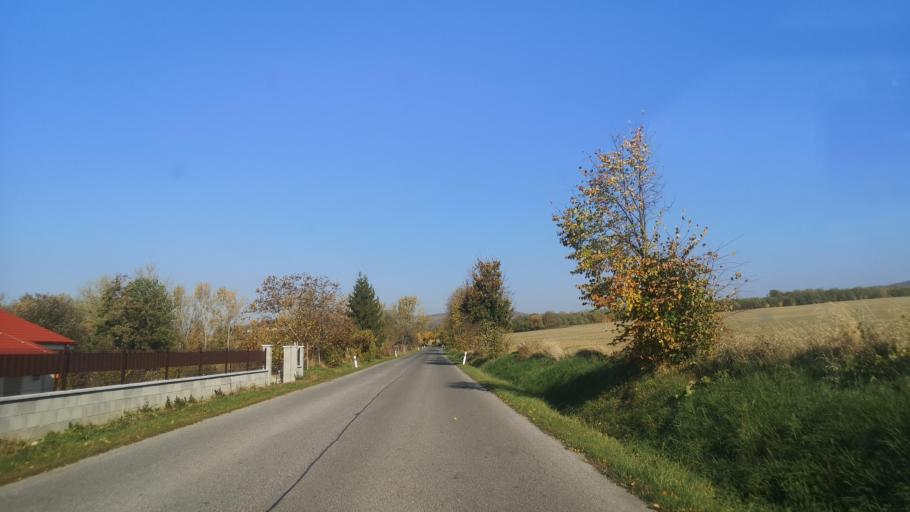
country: SK
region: Nitriansky
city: Zlate Moravce
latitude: 48.4210
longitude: 18.4203
